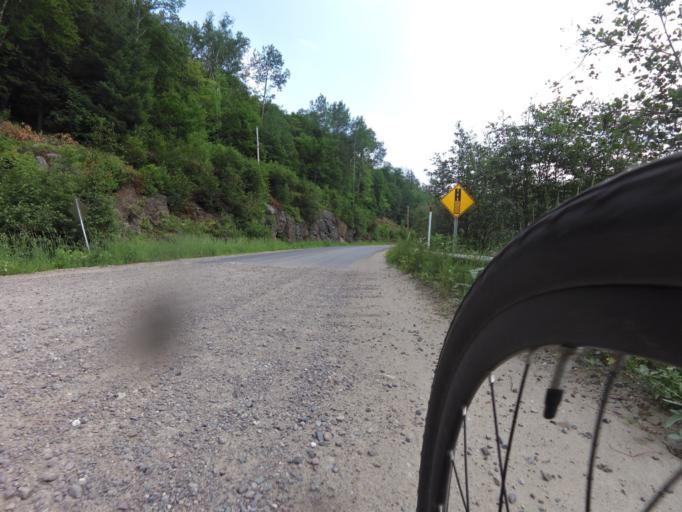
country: CA
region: Quebec
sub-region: Laurentides
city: Brownsburg-Chatham
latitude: 45.9137
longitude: -74.5975
